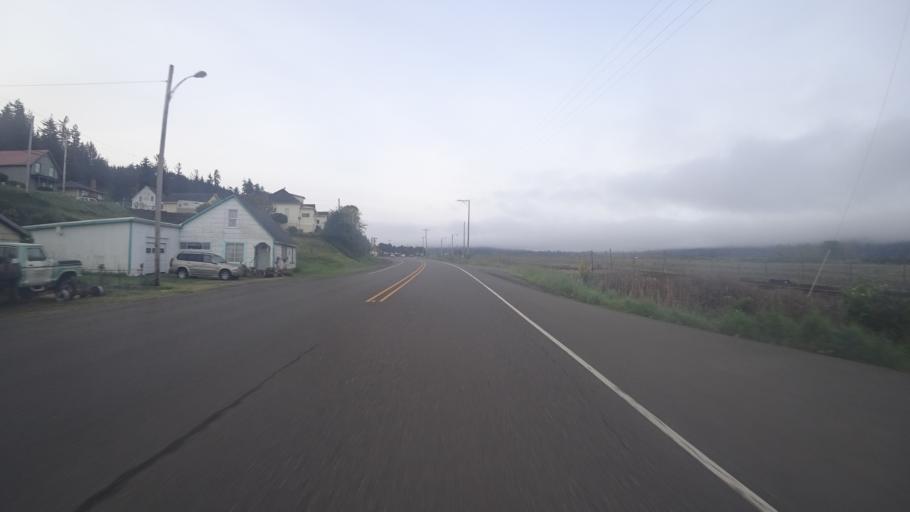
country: US
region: Oregon
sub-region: Douglas County
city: Reedsport
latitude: 43.7340
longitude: -124.1115
